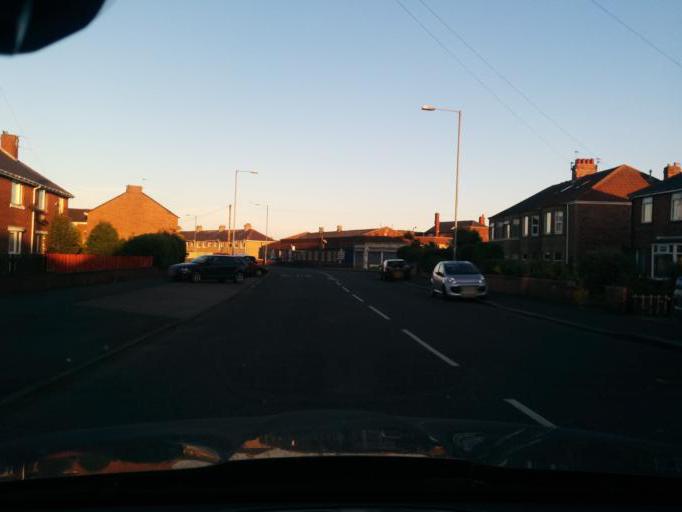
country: GB
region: England
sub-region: Northumberland
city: Newbiggin-by-the-Sea
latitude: 55.1885
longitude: -1.5213
